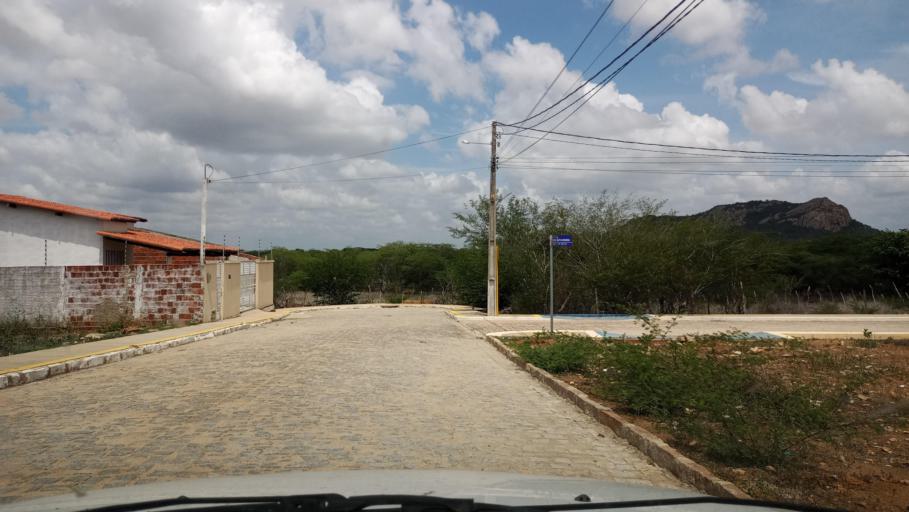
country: BR
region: Rio Grande do Norte
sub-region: Tangara
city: Tangara
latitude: -6.1115
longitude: -35.7166
